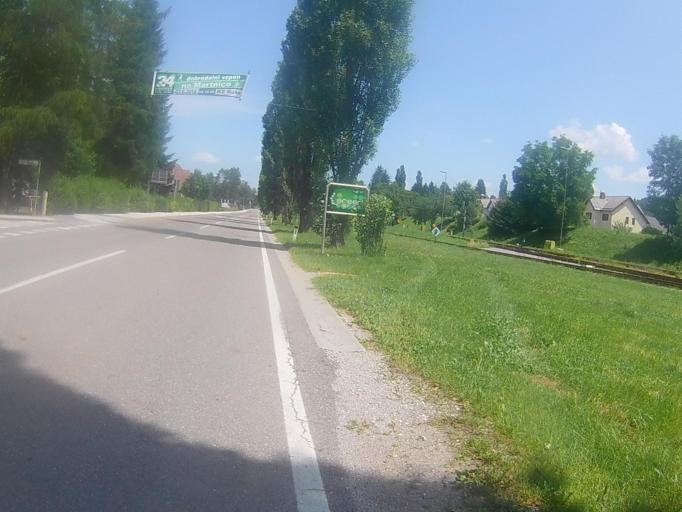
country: SI
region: Ruse
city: Ruse
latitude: 46.5420
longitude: 15.5062
